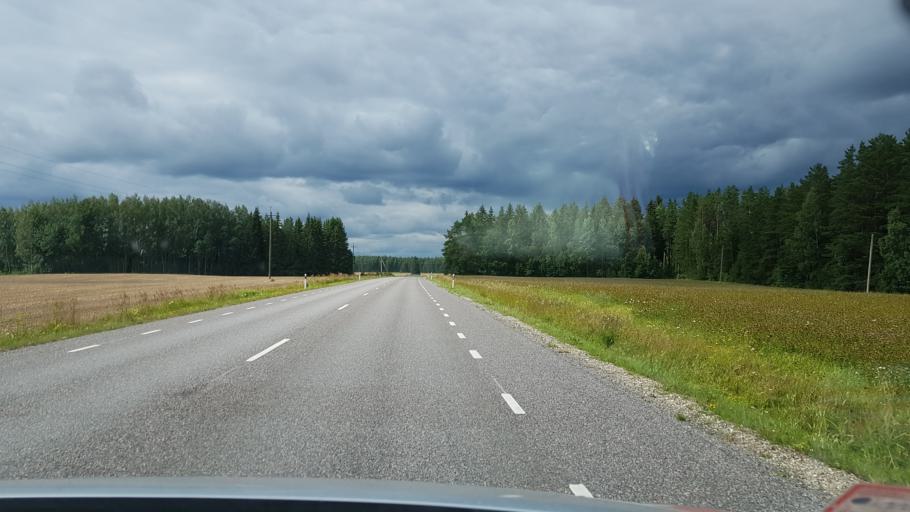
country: EE
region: Polvamaa
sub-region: Raepina vald
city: Rapina
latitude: 58.0995
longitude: 27.3150
